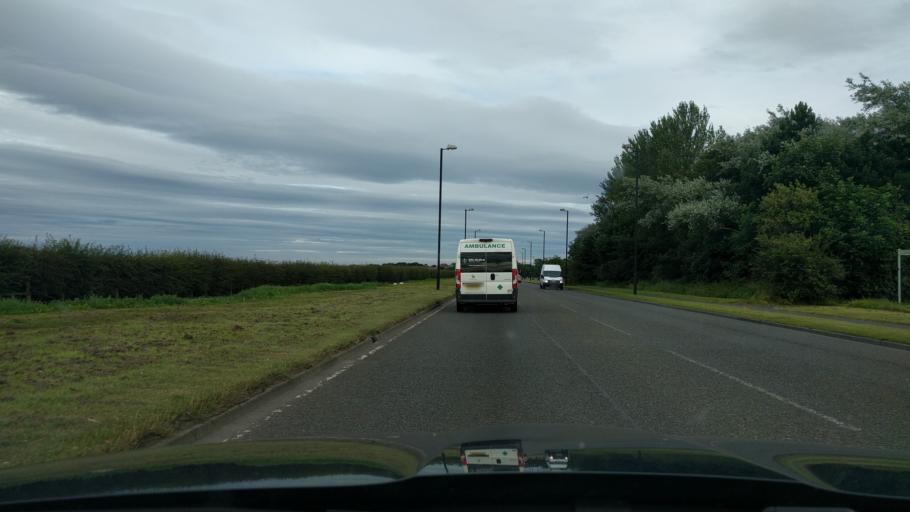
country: GB
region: England
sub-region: Borough of North Tyneside
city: Shiremoor
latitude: 55.0272
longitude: -1.5034
